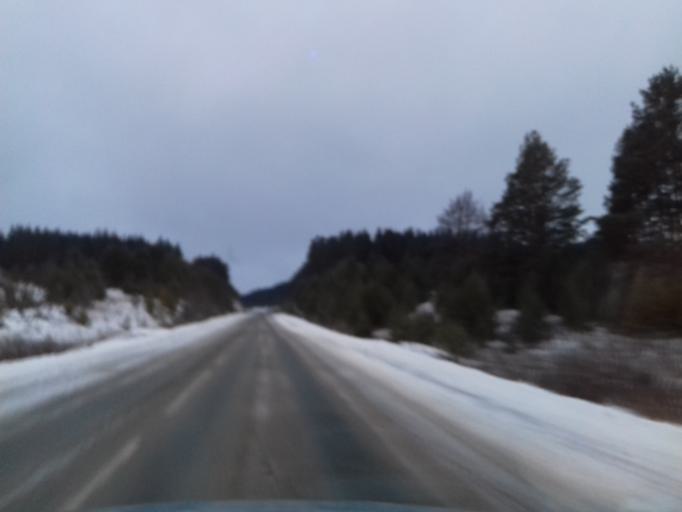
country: RU
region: Bashkortostan
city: Verkhniy Avzyan
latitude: 53.5047
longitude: 57.6748
